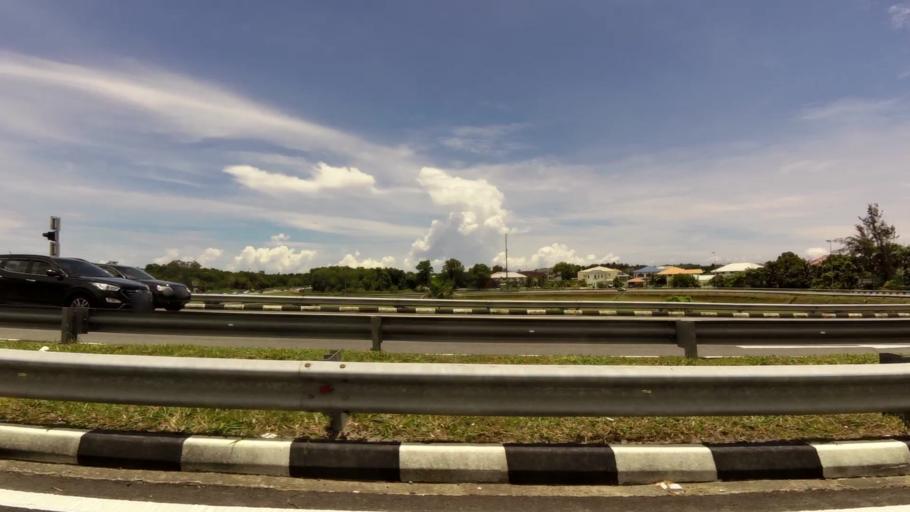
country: BN
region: Brunei and Muara
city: Bandar Seri Begawan
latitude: 4.9428
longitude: 114.9099
